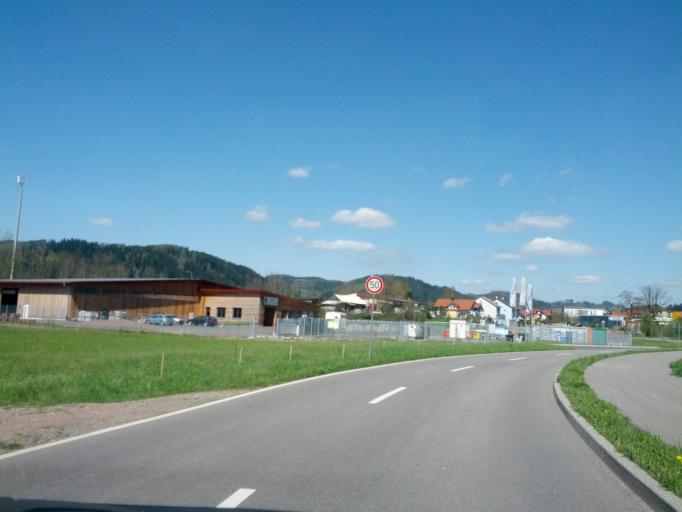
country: DE
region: Baden-Wuerttemberg
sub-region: Freiburg Region
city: Gutach im Breisgau
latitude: 48.1194
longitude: 8.0010
